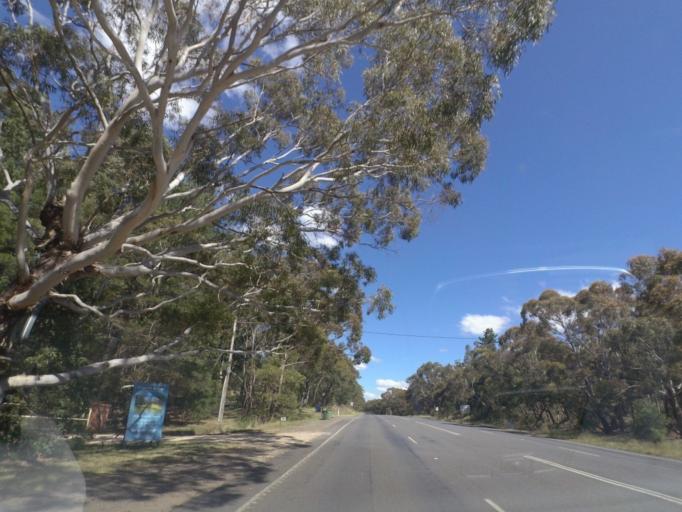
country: AU
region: Victoria
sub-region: Hume
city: Sunbury
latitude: -37.4409
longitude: 144.5662
